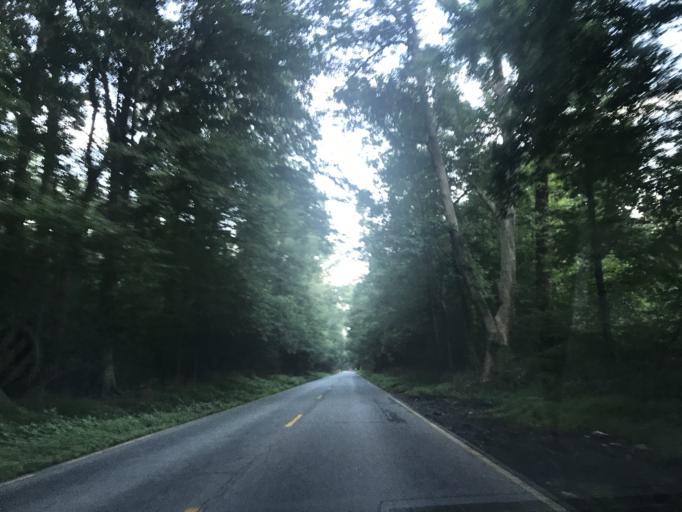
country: US
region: Maryland
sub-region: Cecil County
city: Rising Sun
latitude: 39.6457
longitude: -76.1513
